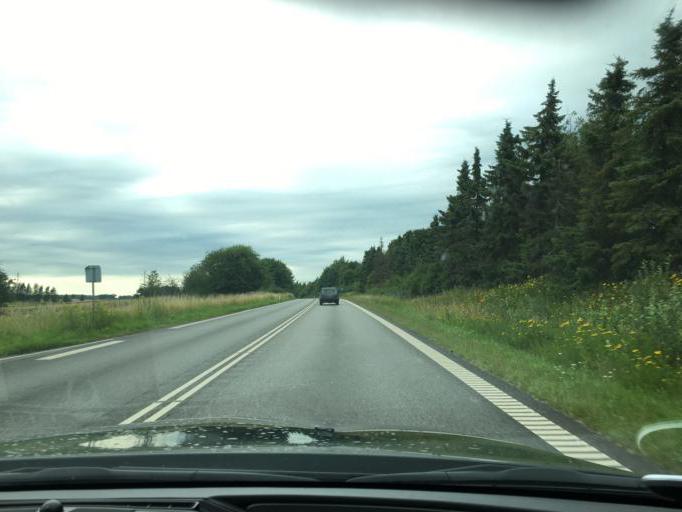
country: DK
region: Capital Region
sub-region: Rudersdal Kommune
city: Birkerod
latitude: 55.8865
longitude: 12.4495
